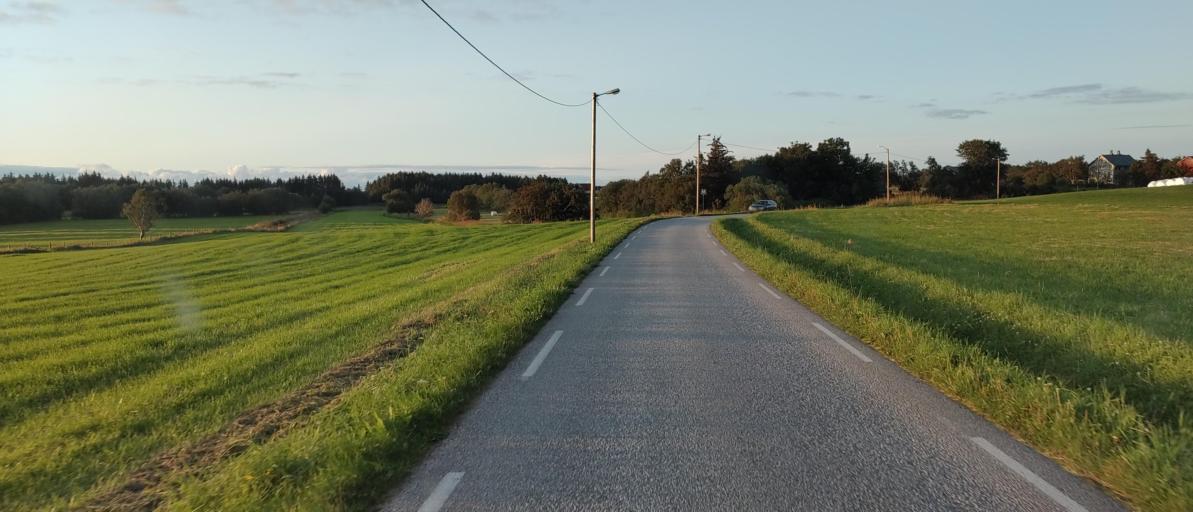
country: NO
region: More og Romsdal
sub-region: Fraena
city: Elnesvagen
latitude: 62.9895
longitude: 7.2113
